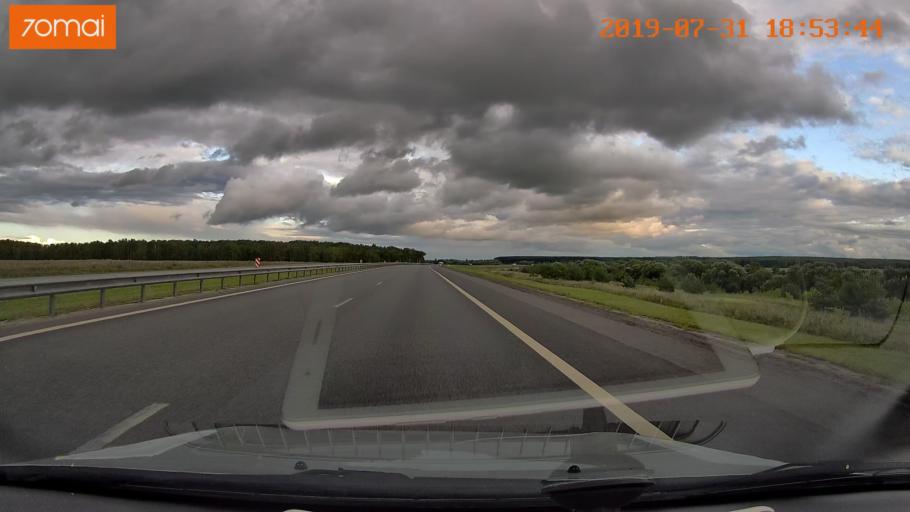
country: RU
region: Moskovskaya
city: Raduzhnyy
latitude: 55.1994
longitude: 38.6586
